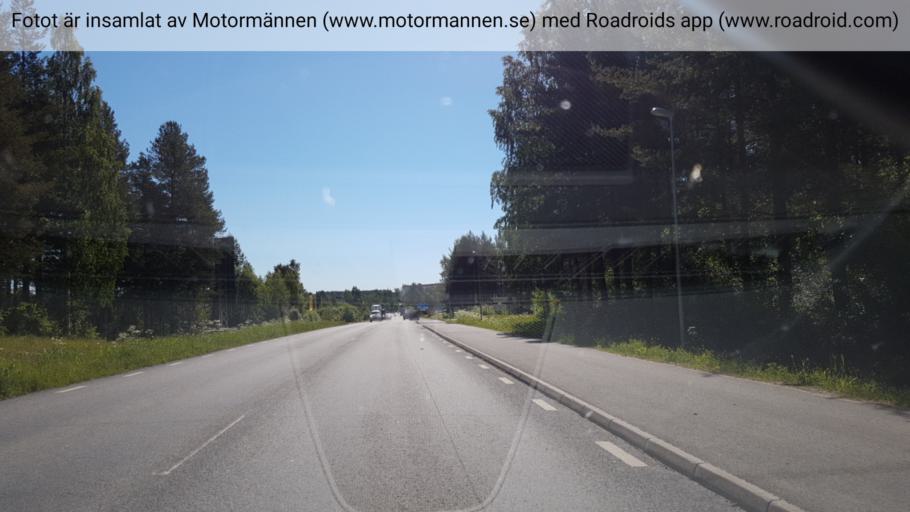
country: SE
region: Norrbotten
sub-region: Bodens Kommun
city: Boden
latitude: 65.8248
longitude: 21.6619
